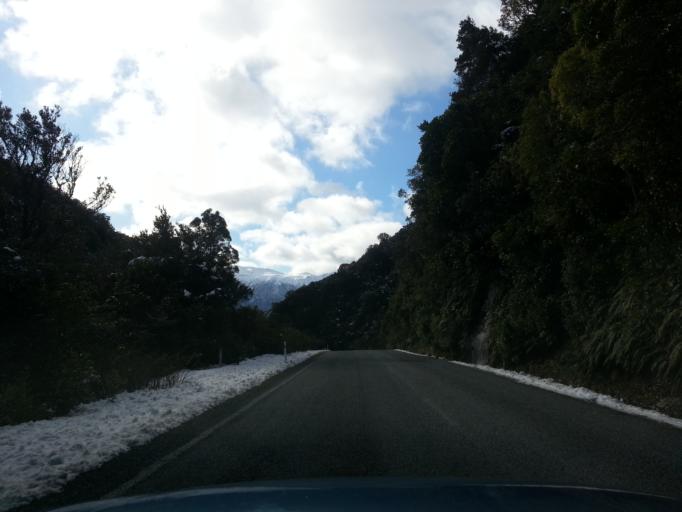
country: NZ
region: West Coast
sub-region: Grey District
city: Greymouth
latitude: -42.8605
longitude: 171.5587
